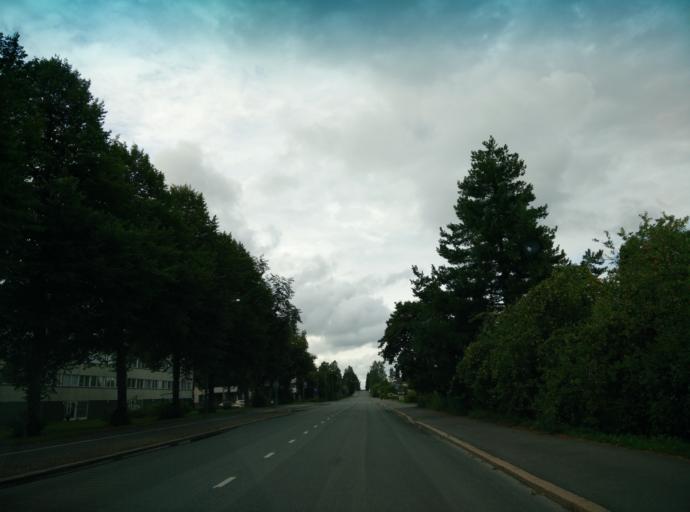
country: FI
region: Haeme
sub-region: Haemeenlinna
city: Haemeenlinna
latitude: 60.9978
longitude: 24.4294
